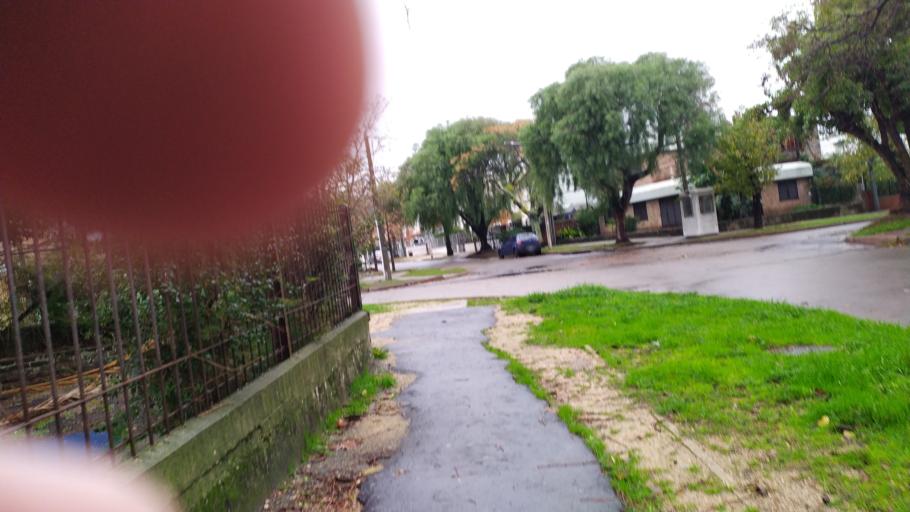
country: UY
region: Canelones
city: Paso de Carrasco
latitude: -34.8930
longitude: -56.0989
